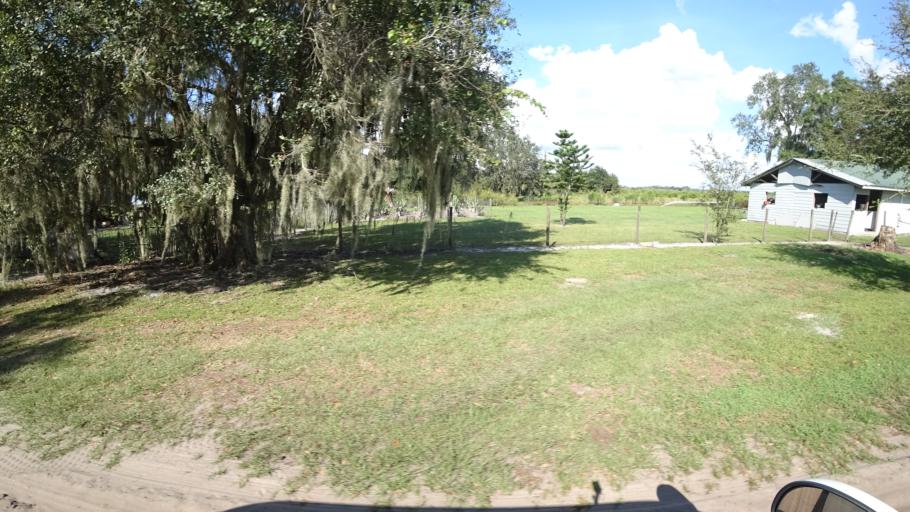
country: US
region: Florida
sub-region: DeSoto County
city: Arcadia
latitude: 27.3093
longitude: -82.0929
